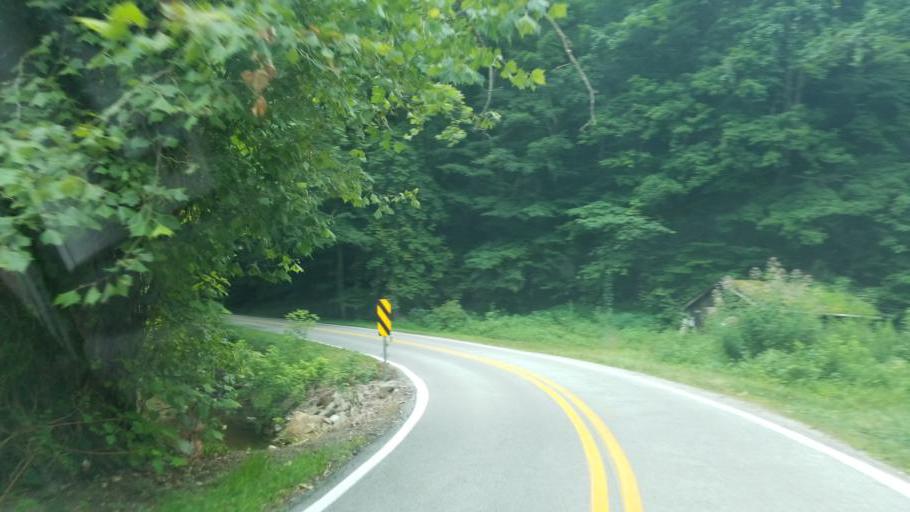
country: US
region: West Virginia
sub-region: Kanawha County
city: Alum Creek
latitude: 38.2810
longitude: -81.7768
